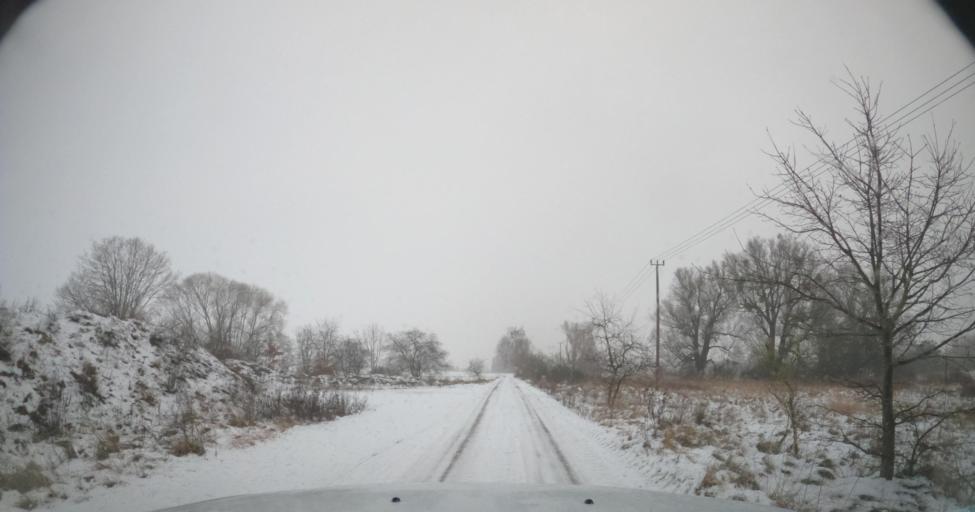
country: PL
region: West Pomeranian Voivodeship
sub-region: Powiat kamienski
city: Golczewo
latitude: 53.7832
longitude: 14.9555
